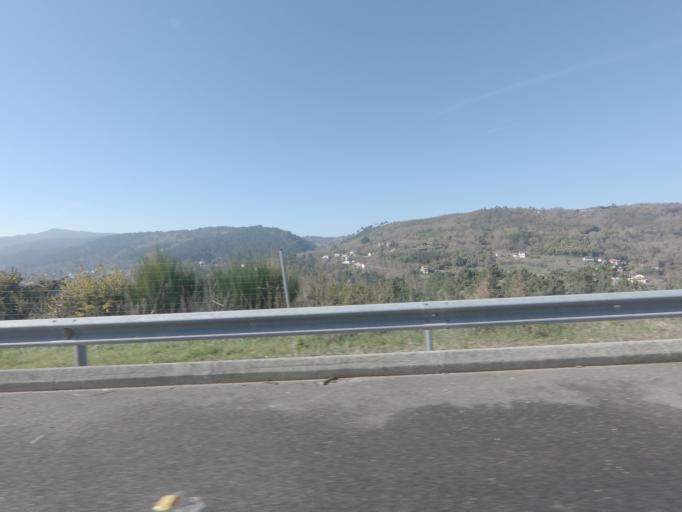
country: ES
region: Galicia
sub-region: Provincia de Ourense
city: Punxin
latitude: 42.3843
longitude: -7.9894
